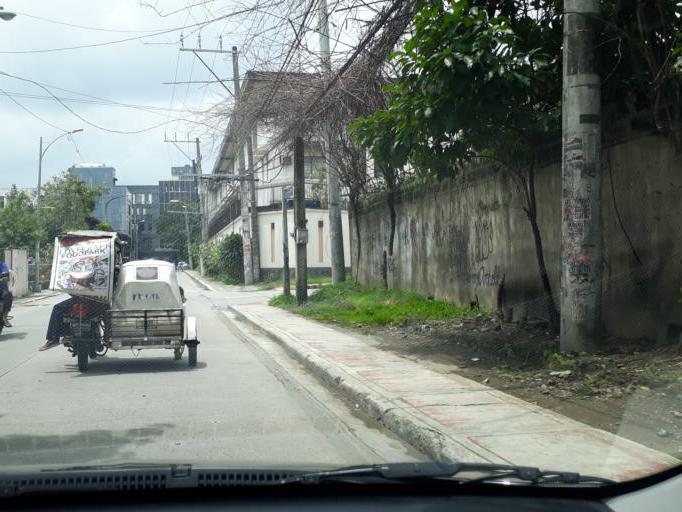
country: PH
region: Metro Manila
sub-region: San Juan
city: San Juan
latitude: 14.6231
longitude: 121.0388
